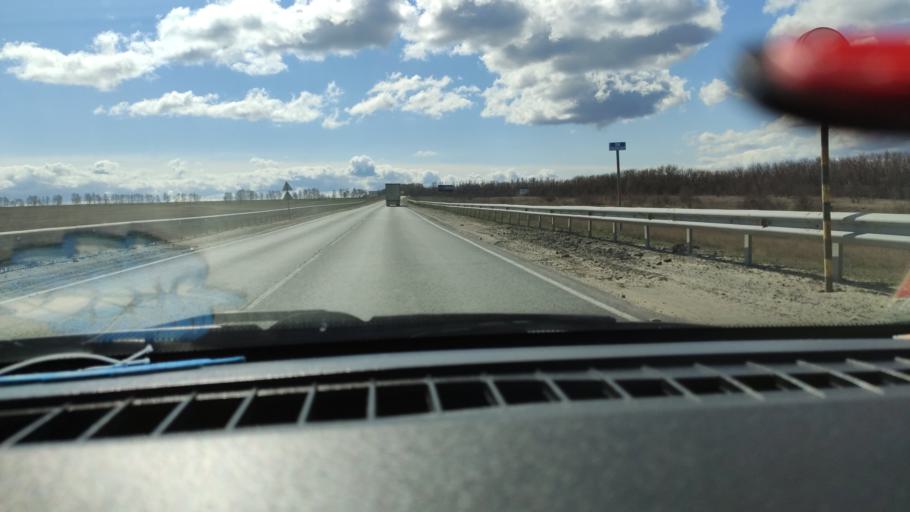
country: RU
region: Saratov
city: Dukhovnitskoye
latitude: 52.7304
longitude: 48.2585
